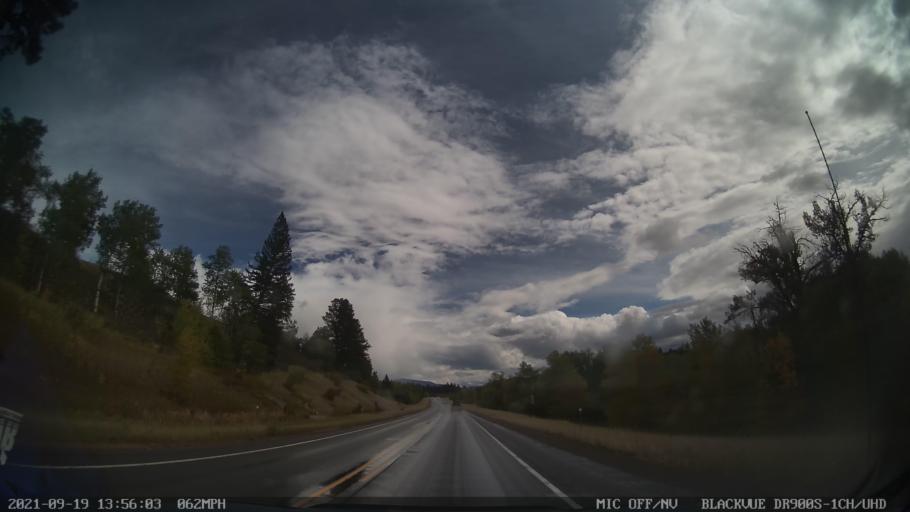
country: US
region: Montana
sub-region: Lewis and Clark County
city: Lincoln
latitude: 47.0178
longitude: -113.0878
